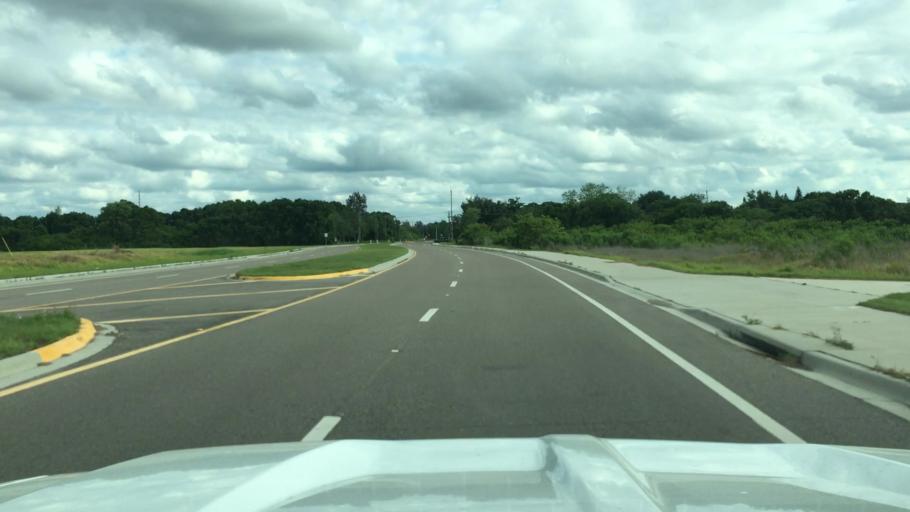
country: US
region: Florida
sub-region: Hillsborough County
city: Ruskin
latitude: 27.7194
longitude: -82.4024
